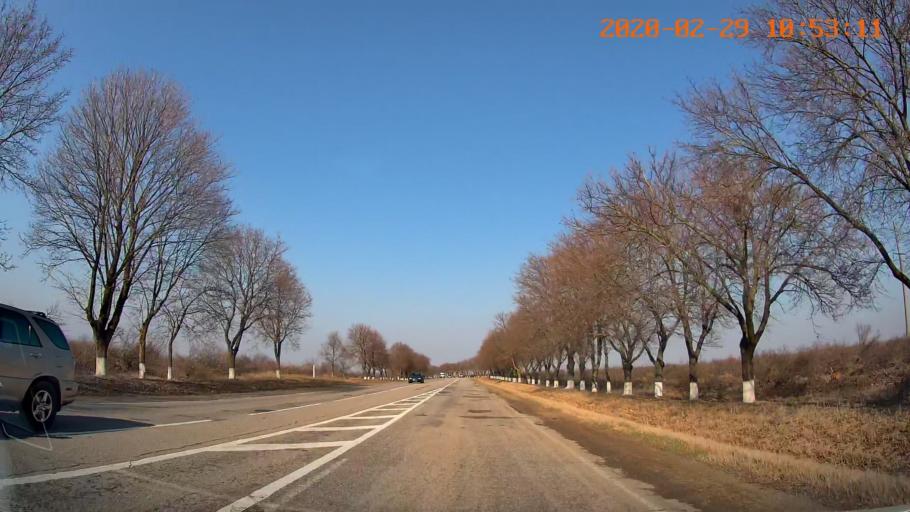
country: MD
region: Telenesti
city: Grigoriopol
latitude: 47.1132
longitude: 29.3397
